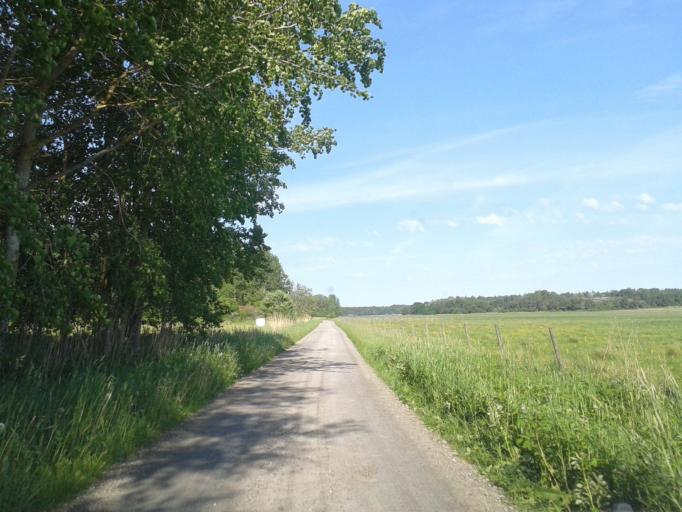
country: SE
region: Vaestra Goetaland
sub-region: Stromstads Kommun
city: Stroemstad
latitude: 58.8625
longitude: 11.2187
